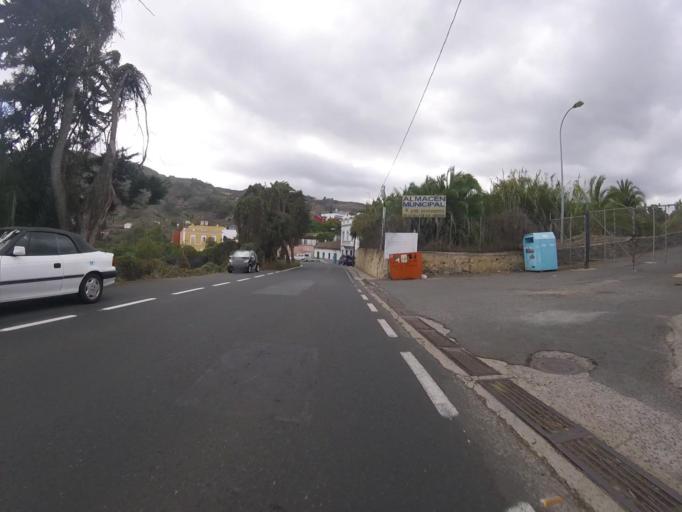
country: ES
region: Canary Islands
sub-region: Provincia de Las Palmas
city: Santa Brigida
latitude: 28.0257
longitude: -15.5046
